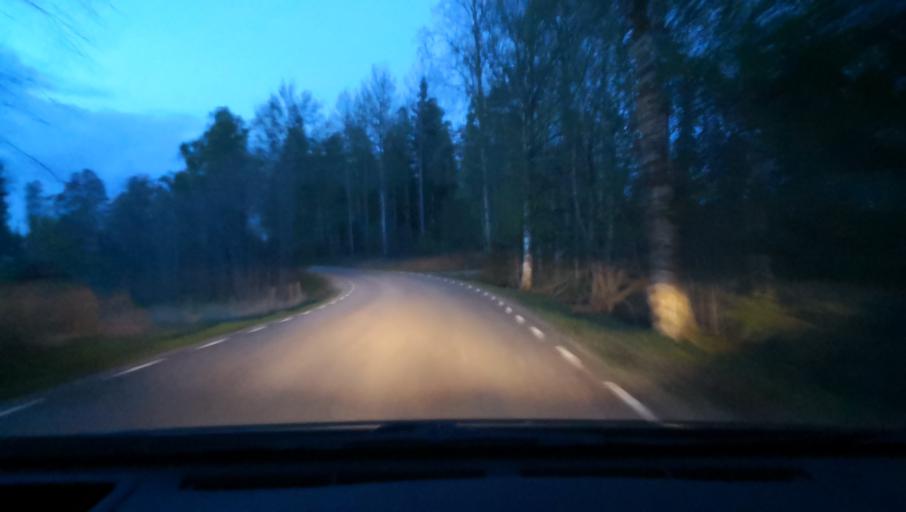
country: SE
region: OErebro
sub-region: Orebro Kommun
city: Vintrosa
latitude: 59.1876
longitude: 15.0423
